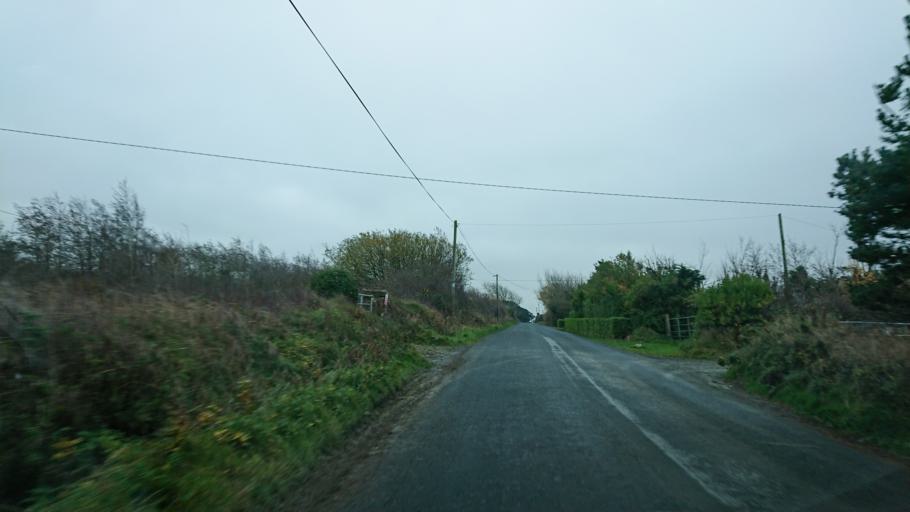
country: IE
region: Munster
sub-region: Waterford
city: Dunmore East
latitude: 52.1673
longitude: -7.0667
